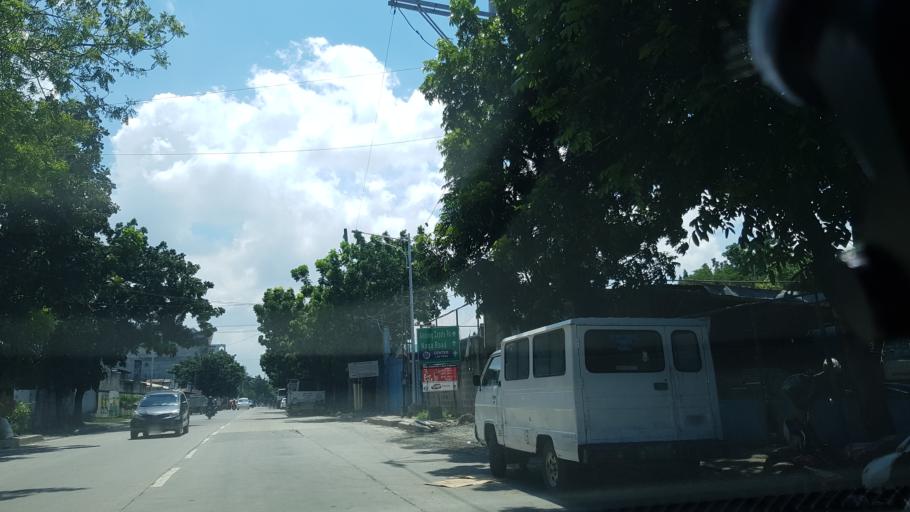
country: PH
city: Sambayanihan People's Village
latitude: 14.4657
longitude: 120.9963
